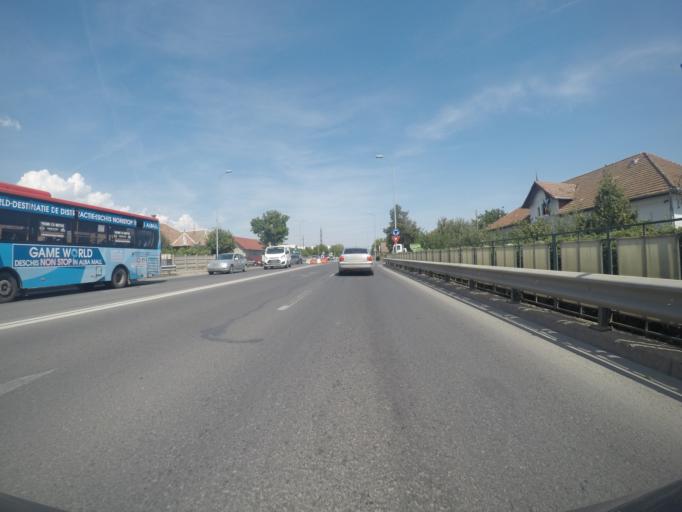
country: RO
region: Alba
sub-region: Municipiul Alba Iulia
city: Barabant
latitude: 46.0920
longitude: 23.5954
